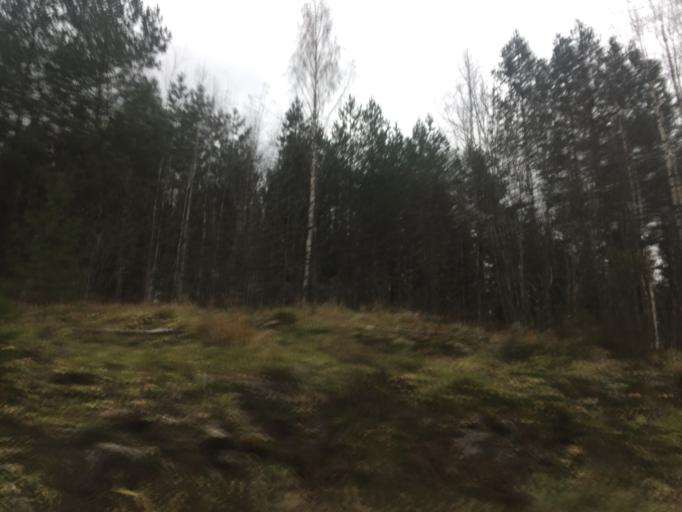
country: RU
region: Republic of Karelia
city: Lakhdenpokh'ya
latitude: 61.4315
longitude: 30.1381
